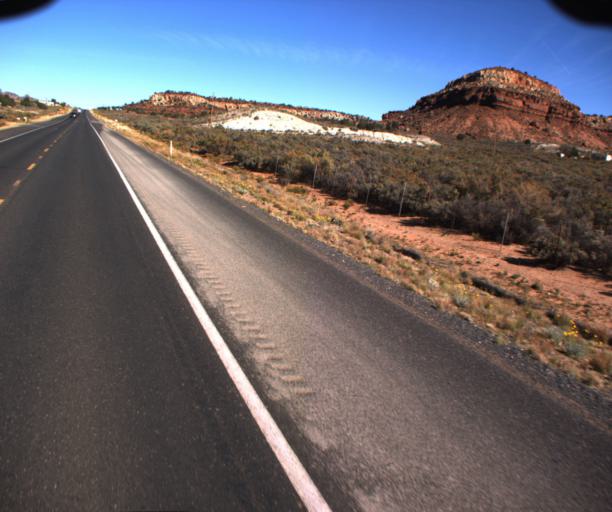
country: US
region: Arizona
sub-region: Coconino County
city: Fredonia
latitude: 36.9815
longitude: -112.5293
